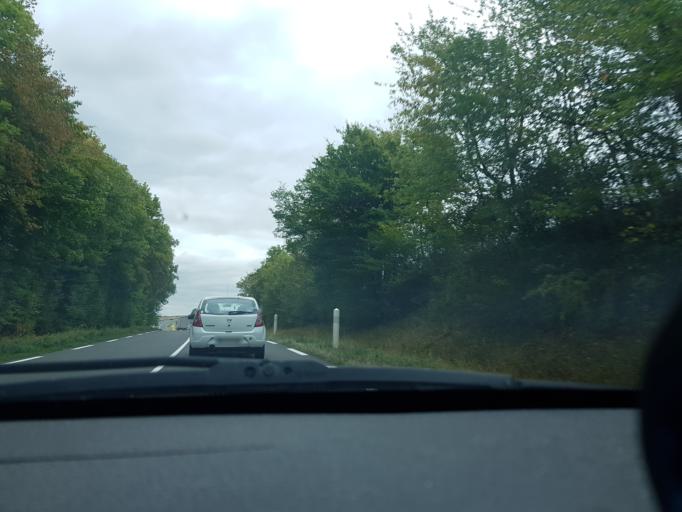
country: FR
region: Lorraine
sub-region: Departement de la Moselle
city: Chateau-Salins
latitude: 48.7775
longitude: 6.4680
